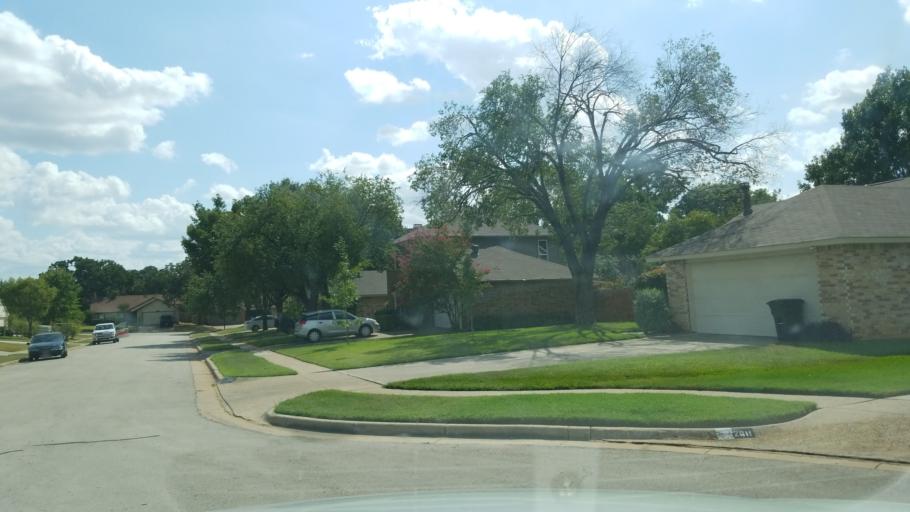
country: US
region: Texas
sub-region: Tarrant County
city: Euless
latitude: 32.8752
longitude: -97.0857
